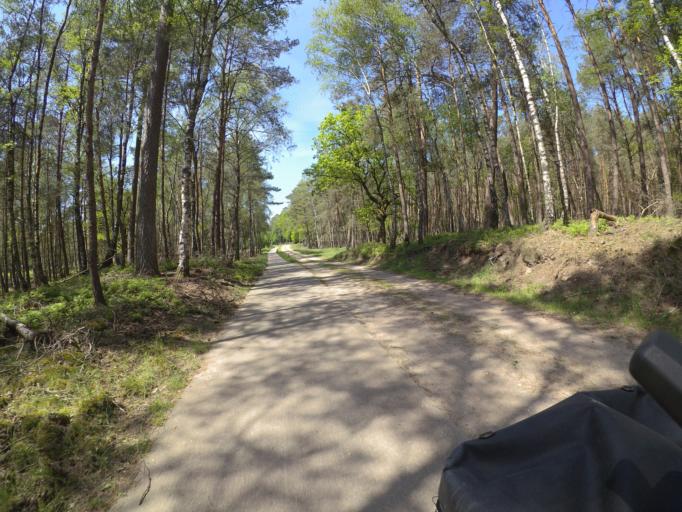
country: NL
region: Gelderland
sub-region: Gemeente Apeldoorn
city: Loenen
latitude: 52.0657
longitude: 6.0032
